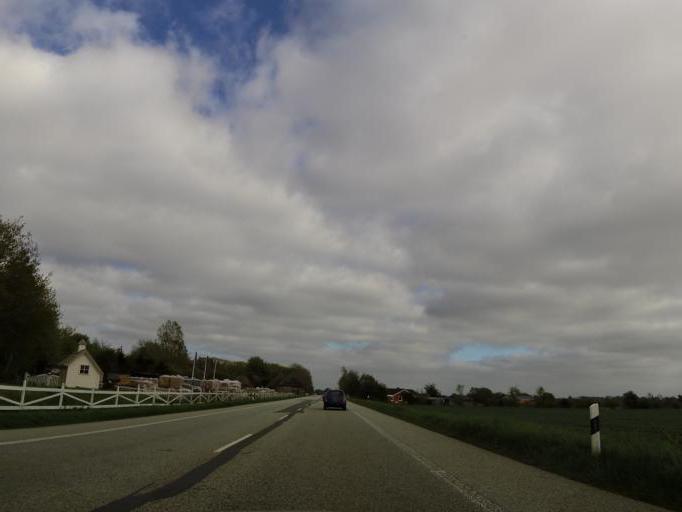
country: DE
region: Schleswig-Holstein
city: Risum-Lindholm
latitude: 54.7684
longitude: 8.8642
